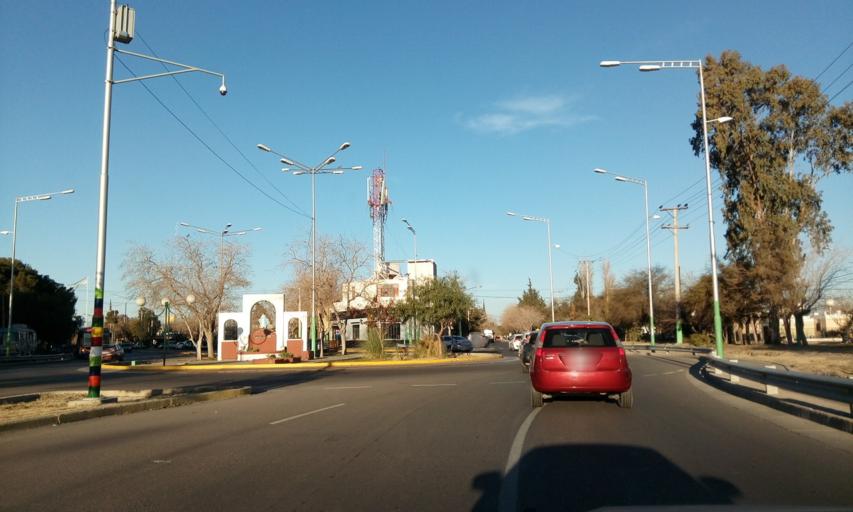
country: AR
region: San Juan
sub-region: Departamento de Rivadavia
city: Rivadavia
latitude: -31.5309
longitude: -68.5978
